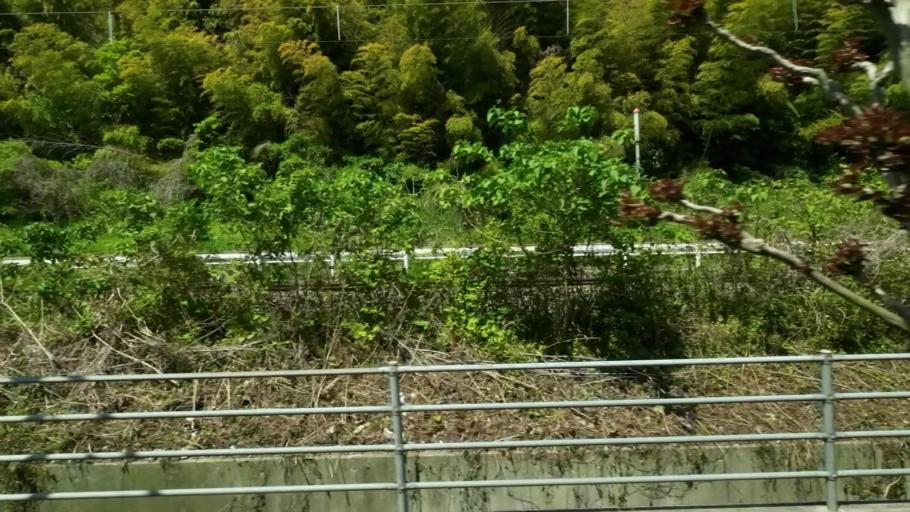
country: JP
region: Ehime
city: Hojo
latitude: 34.0776
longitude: 132.9854
